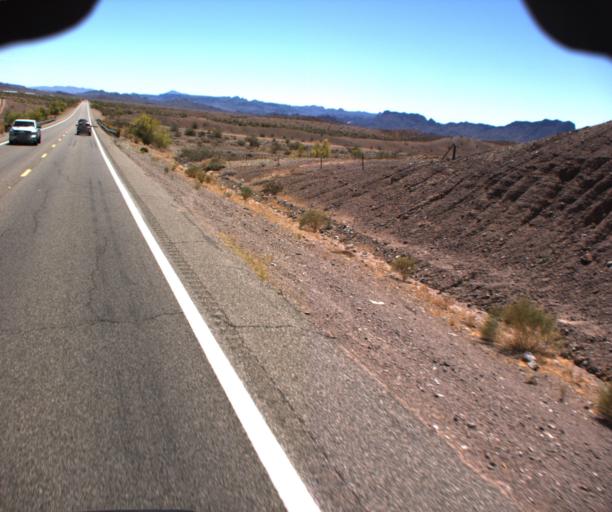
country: US
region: Arizona
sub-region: Mohave County
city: Lake Havasu City
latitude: 34.4251
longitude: -114.2063
